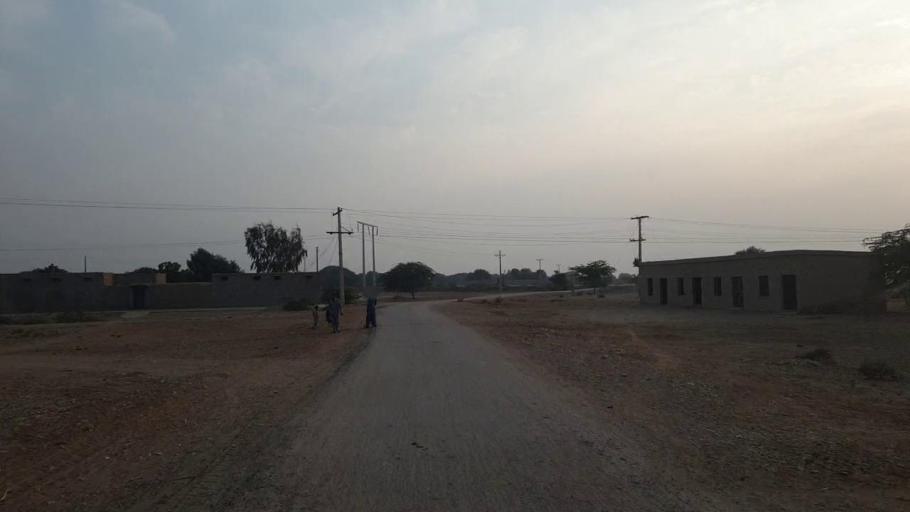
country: PK
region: Sindh
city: Sann
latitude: 26.1636
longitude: 68.0076
